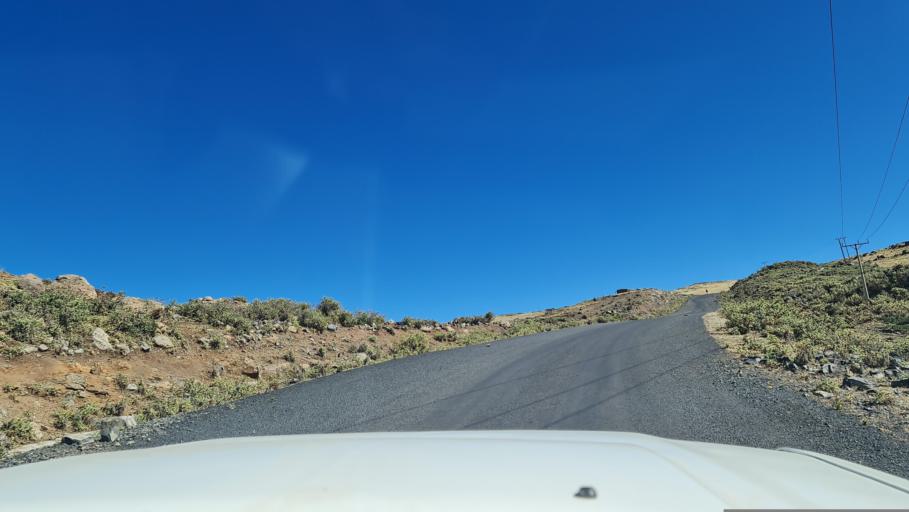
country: ET
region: Amhara
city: Debark'
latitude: 13.1403
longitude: 38.1771
